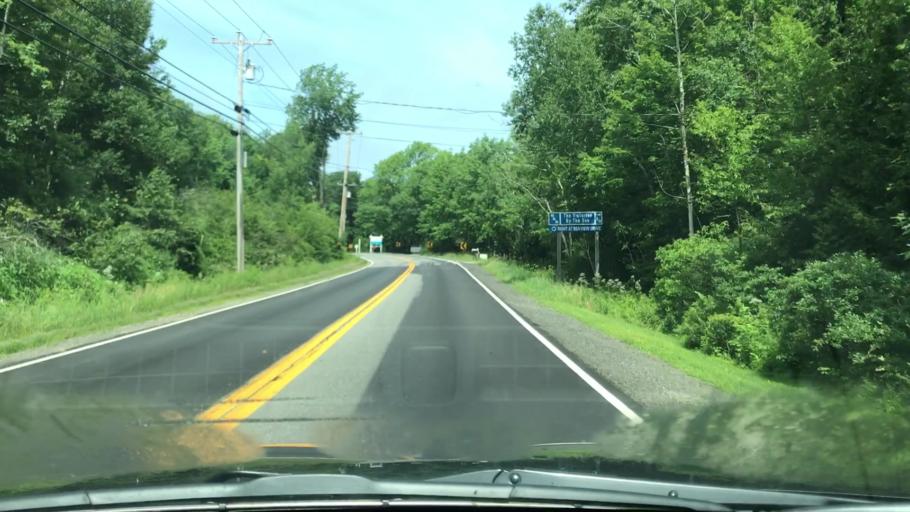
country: US
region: Maine
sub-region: Waldo County
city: Lincolnville
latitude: 44.2625
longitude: -69.0201
